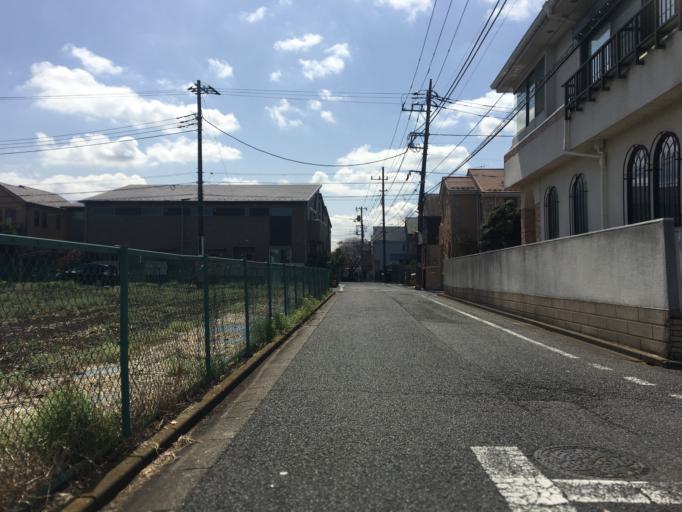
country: JP
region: Tokyo
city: Musashino
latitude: 35.7275
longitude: 139.5952
